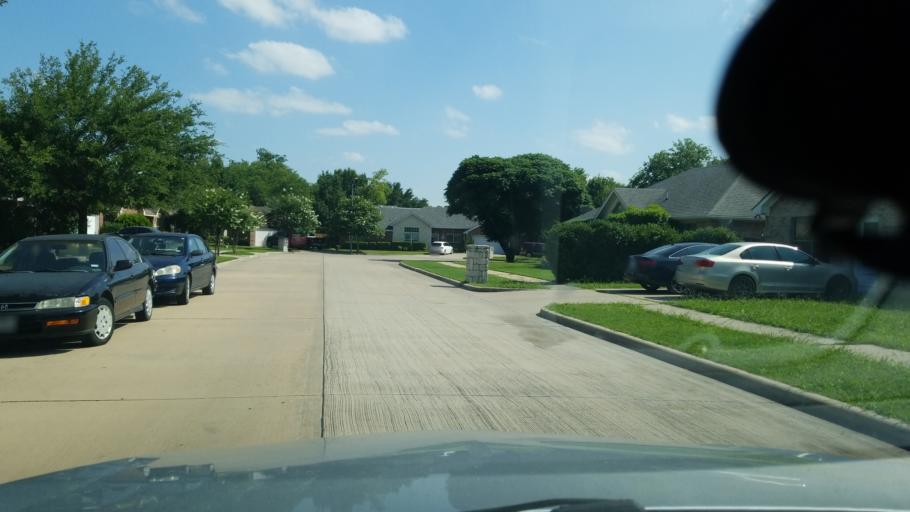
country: US
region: Texas
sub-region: Dallas County
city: Irving
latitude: 32.8147
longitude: -96.9727
